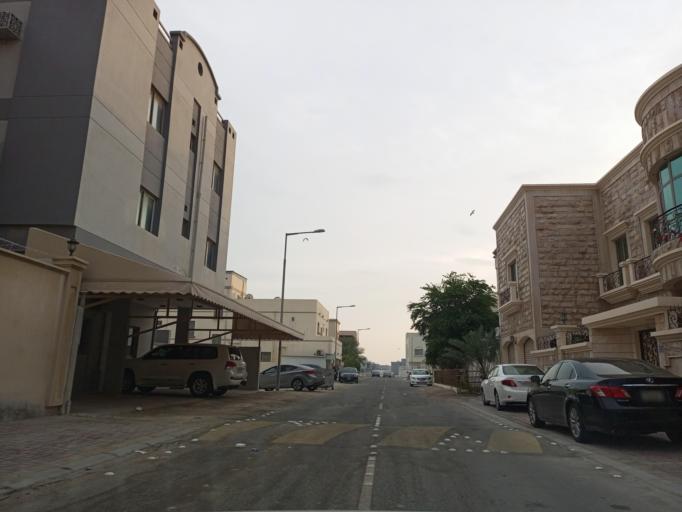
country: BH
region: Muharraq
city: Al Hadd
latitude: 26.2434
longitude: 50.6438
